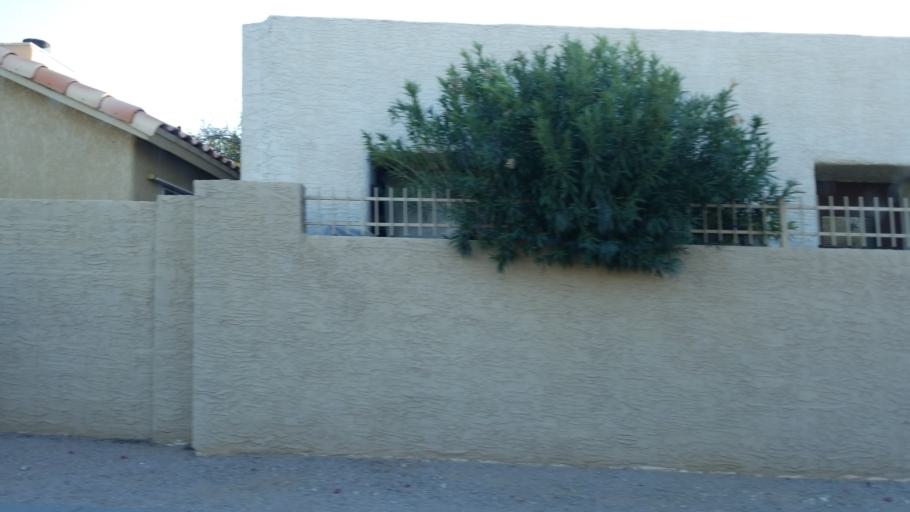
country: US
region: Arizona
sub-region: Maricopa County
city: Scottsdale
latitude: 33.5883
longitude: -111.8415
